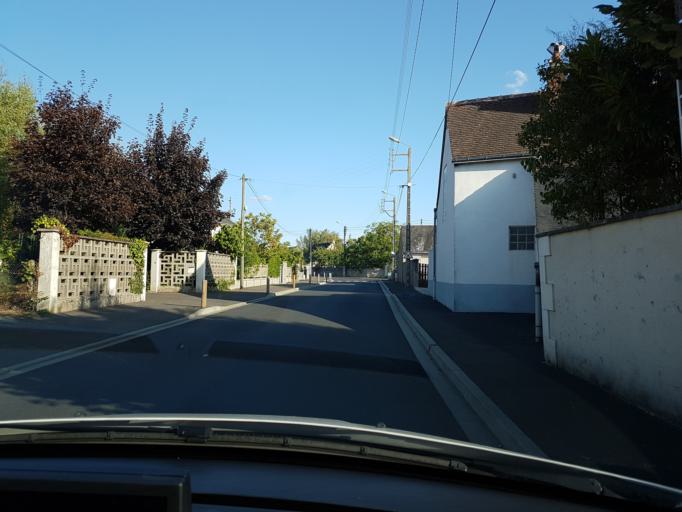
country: FR
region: Centre
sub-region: Departement d'Indre-et-Loire
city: Saint-Avertin
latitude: 47.3565
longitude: 0.7355
